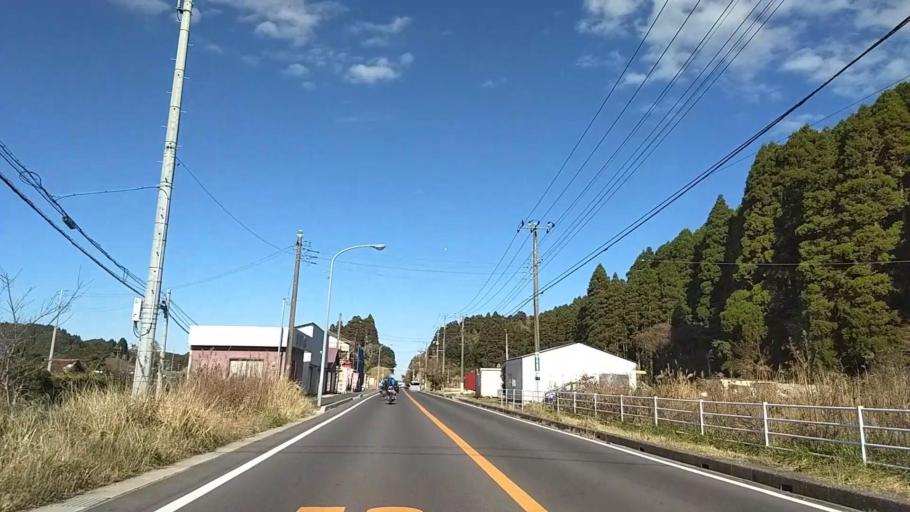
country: JP
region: Chiba
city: Ohara
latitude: 35.2131
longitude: 140.3763
